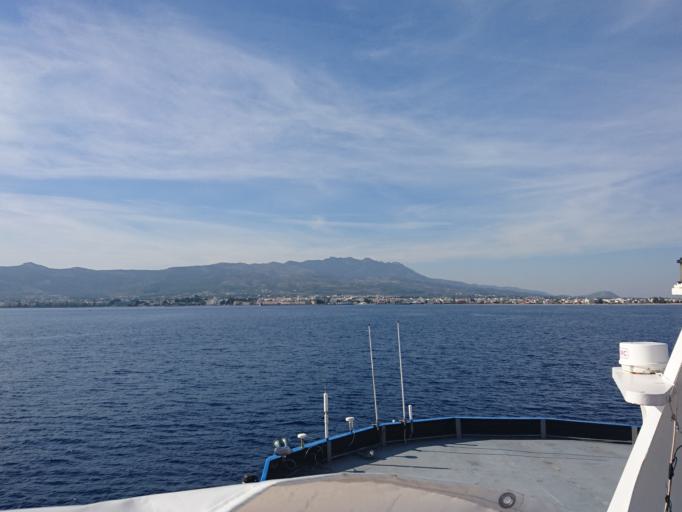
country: GR
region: South Aegean
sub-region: Nomos Dodekanisou
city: Kos
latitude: 36.9086
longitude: 27.3005
